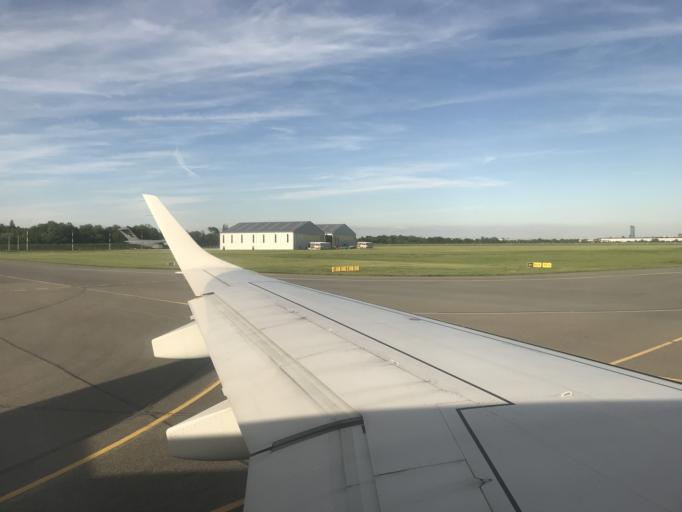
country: PL
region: Lower Silesian Voivodeship
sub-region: Powiat wroclawski
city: Smolec
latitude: 51.1018
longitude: 16.8997
